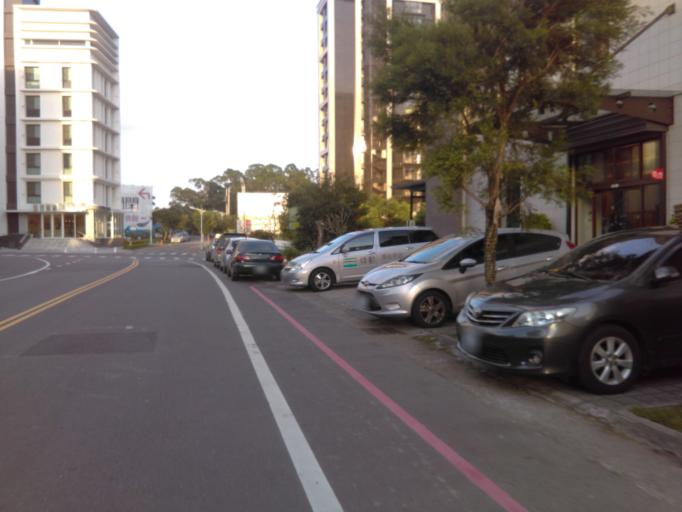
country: TW
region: Taiwan
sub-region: Yilan
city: Yilan
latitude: 24.8318
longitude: 121.7744
